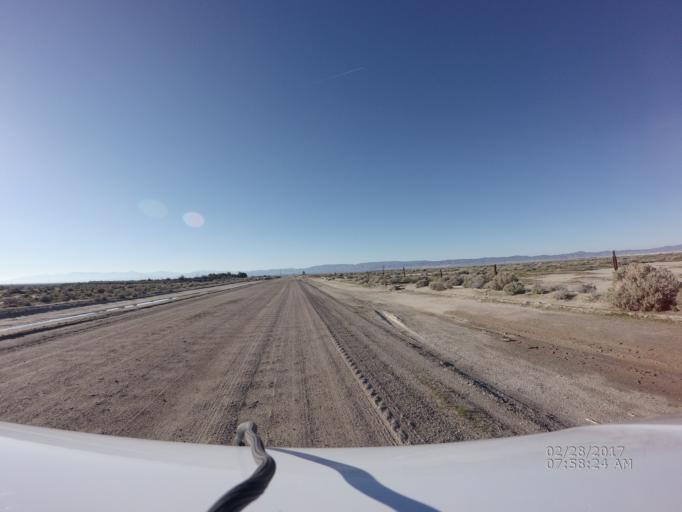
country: US
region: California
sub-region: Kern County
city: Rosamond
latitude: 34.7803
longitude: -118.1847
